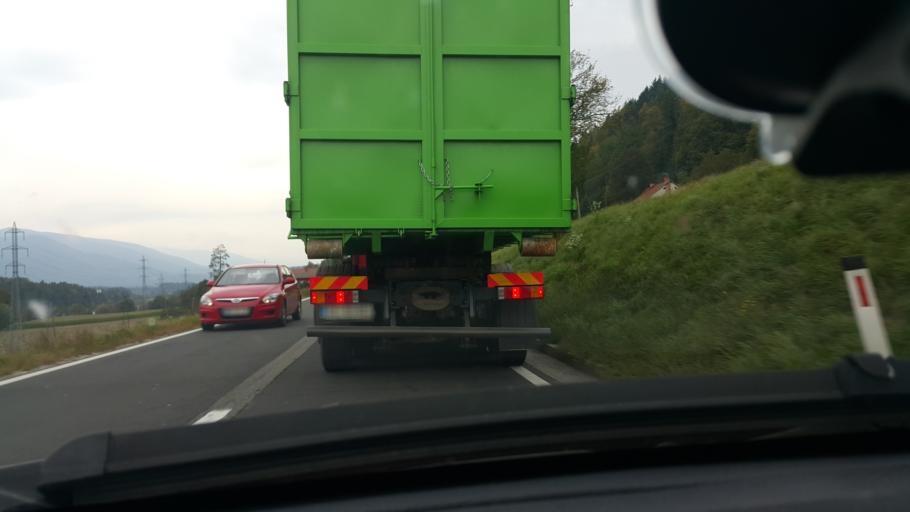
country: SI
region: Ruse
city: Bistrica ob Dravi
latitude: 46.5615
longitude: 15.5427
